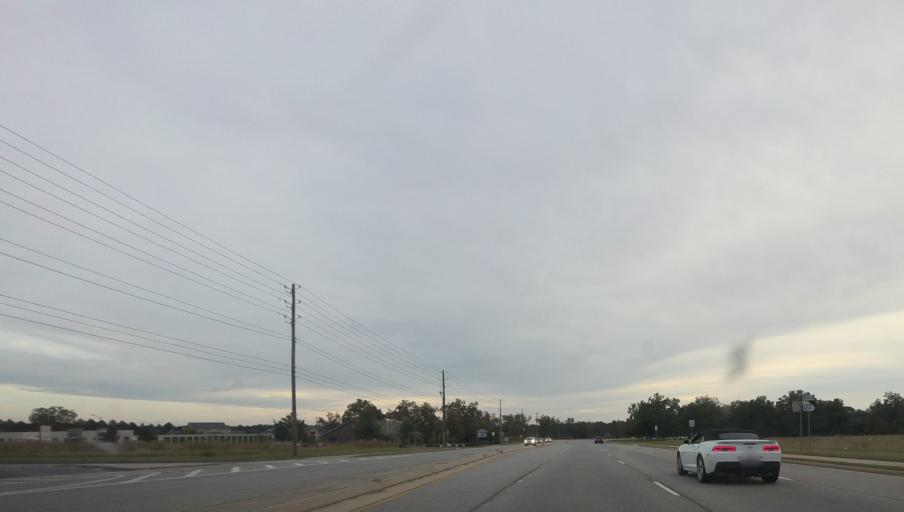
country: US
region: Georgia
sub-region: Houston County
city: Perry
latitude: 32.5047
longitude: -83.6627
